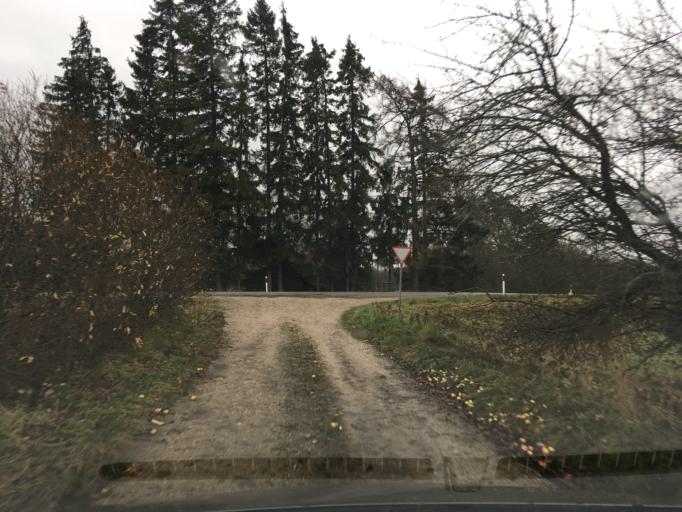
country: EE
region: Laeaene
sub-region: Lihula vald
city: Lihula
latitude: 58.7007
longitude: 23.8565
